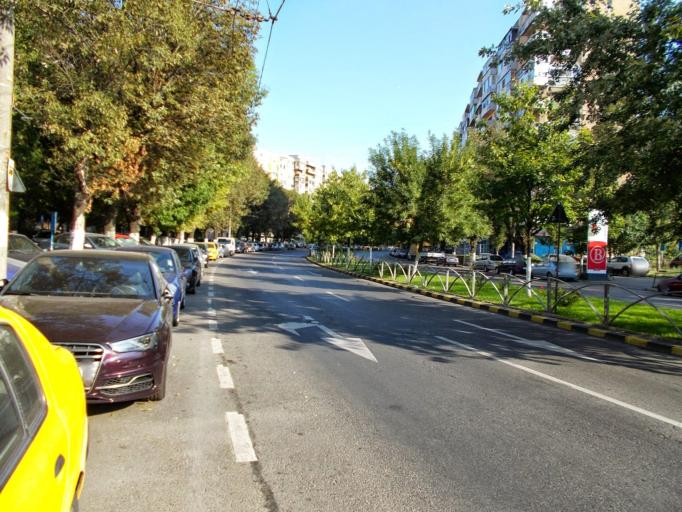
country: RO
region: Bucuresti
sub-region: Municipiul Bucuresti
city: Bucuresti
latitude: 44.3827
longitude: 26.1150
